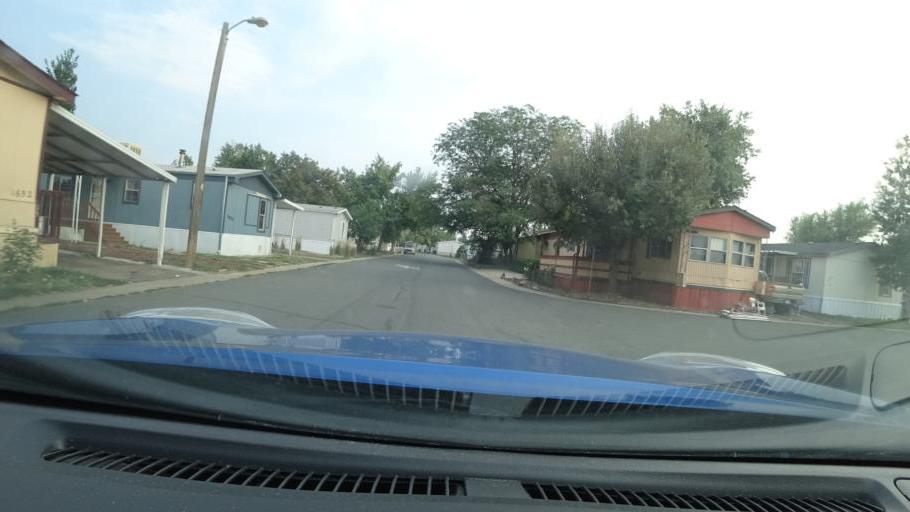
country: US
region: Colorado
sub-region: Adams County
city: Aurora
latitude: 39.7431
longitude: -104.7884
